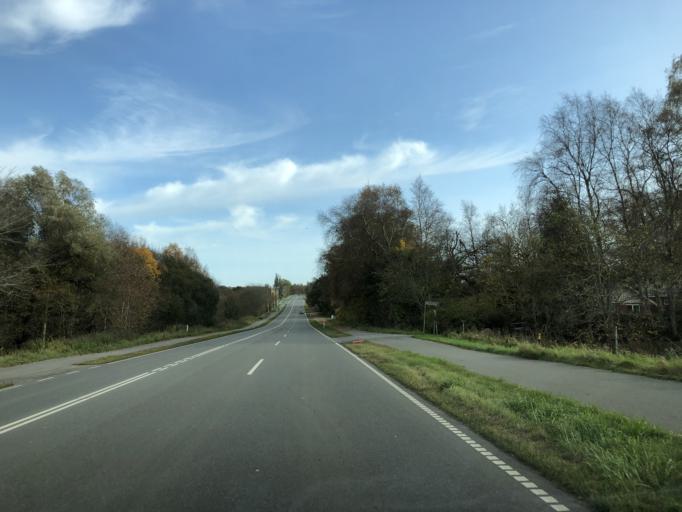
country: DK
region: Capital Region
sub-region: Rudersdal Kommune
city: Birkerod
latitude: 55.8549
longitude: 12.4113
